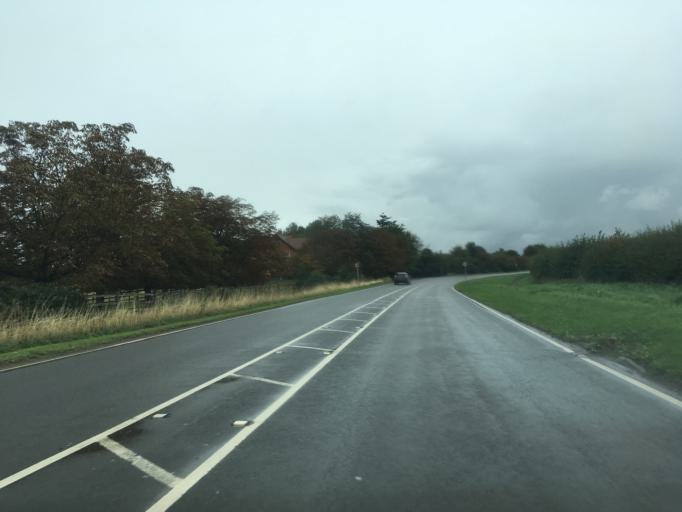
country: GB
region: England
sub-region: Nottinghamshire
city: Ruddington
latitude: 52.8704
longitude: -1.1310
